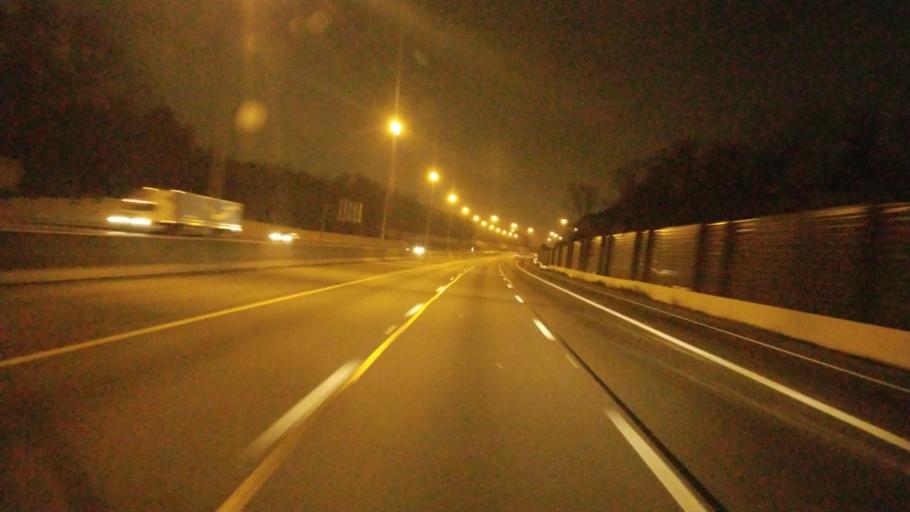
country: US
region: Ohio
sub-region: Franklin County
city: Westerville
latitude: 40.1227
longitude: -82.9729
